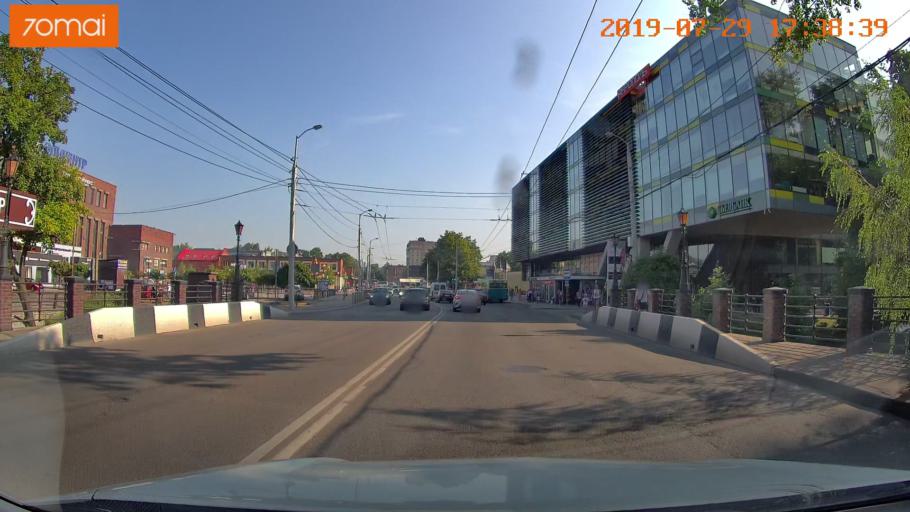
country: RU
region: Kaliningrad
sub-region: Gorod Kaliningrad
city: Kaliningrad
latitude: 54.7219
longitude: 20.5072
